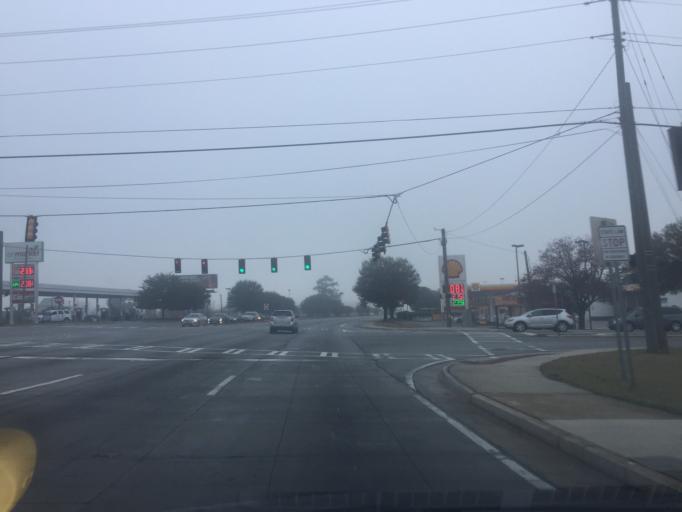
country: US
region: Georgia
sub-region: Chatham County
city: Georgetown
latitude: 31.9810
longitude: -81.1685
